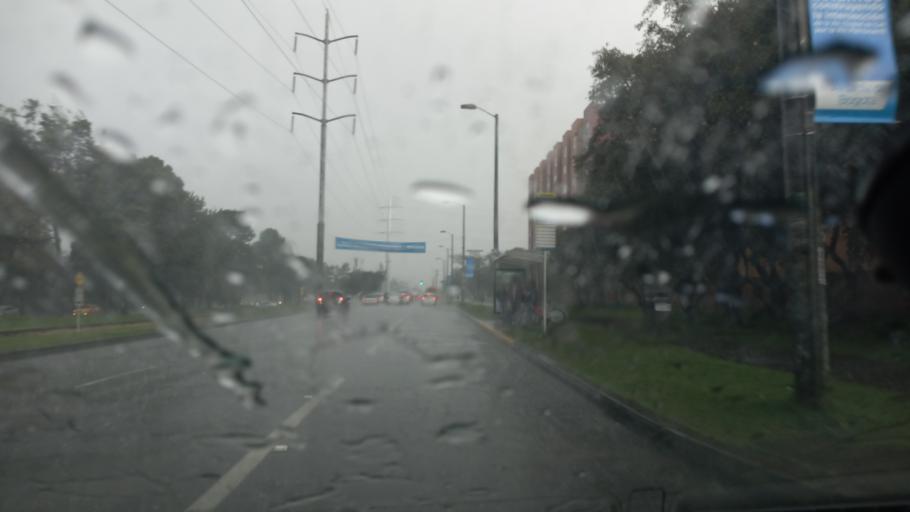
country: CO
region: Bogota D.C.
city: Bogota
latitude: 4.6673
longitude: -74.1322
